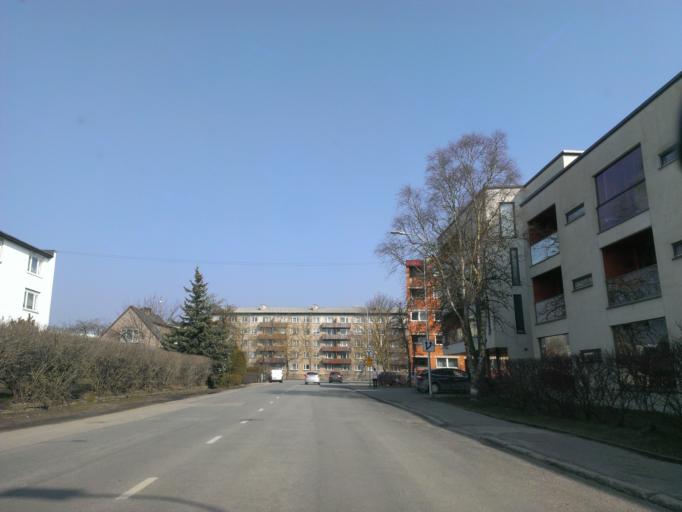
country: EE
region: Saare
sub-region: Kuressaare linn
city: Kuressaare
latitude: 58.2606
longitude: 22.4855
